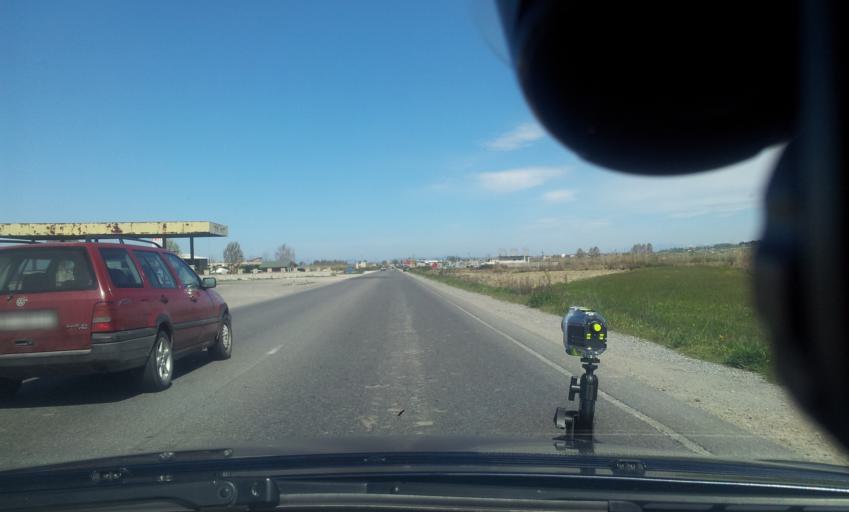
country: AL
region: Durres
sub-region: Rrethi i Krujes
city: Thumane
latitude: 41.5253
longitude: 19.6842
